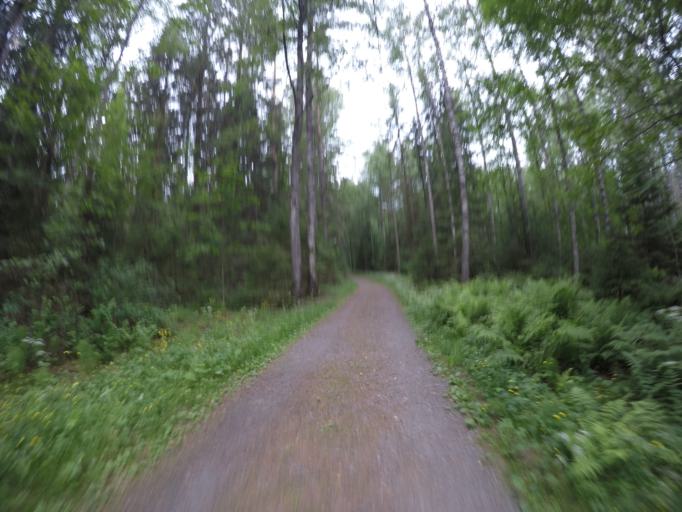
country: FI
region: Haeme
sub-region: Haemeenlinna
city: Haemeenlinna
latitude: 61.0008
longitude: 24.4044
